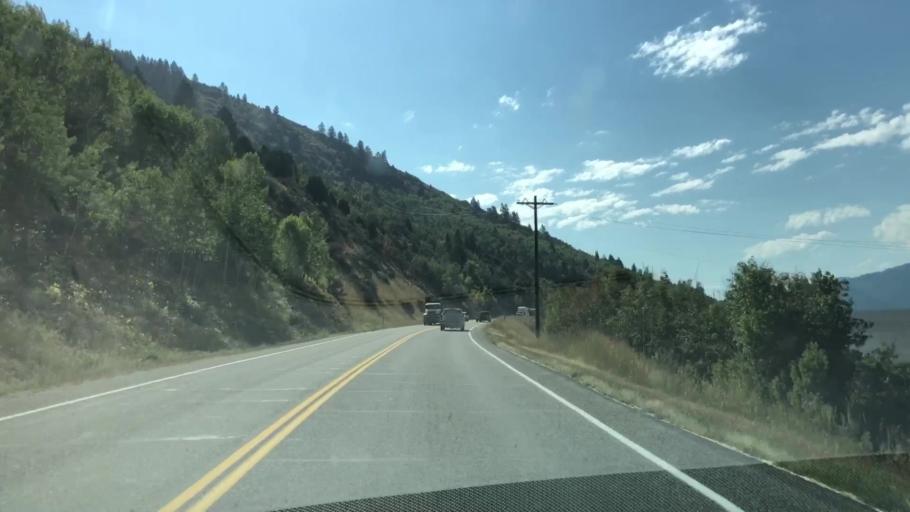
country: US
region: Idaho
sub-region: Teton County
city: Victor
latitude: 43.3423
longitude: -111.2028
